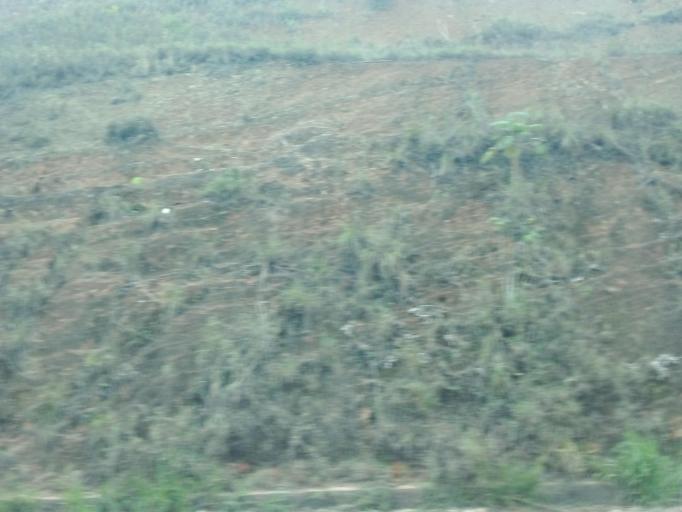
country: BR
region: Minas Gerais
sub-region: Nova Era
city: Nova Era
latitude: -19.6700
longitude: -42.8973
